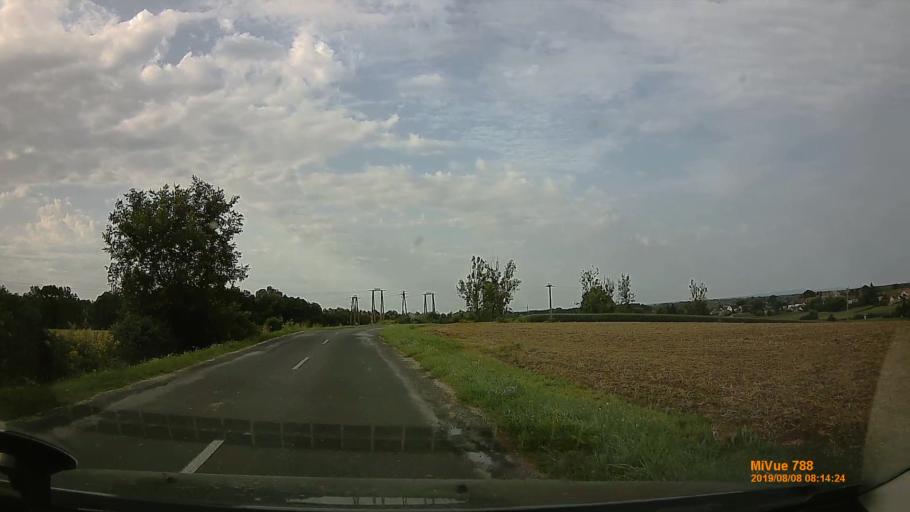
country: HU
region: Zala
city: Murakeresztur
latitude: 46.3990
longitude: 16.8551
